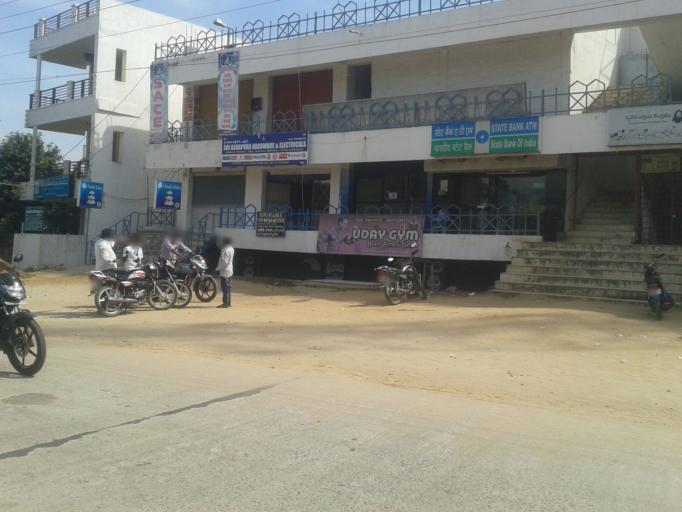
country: IN
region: Andhra Pradesh
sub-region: Chittoor
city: Narasingapuram
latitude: 13.5895
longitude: 79.3195
